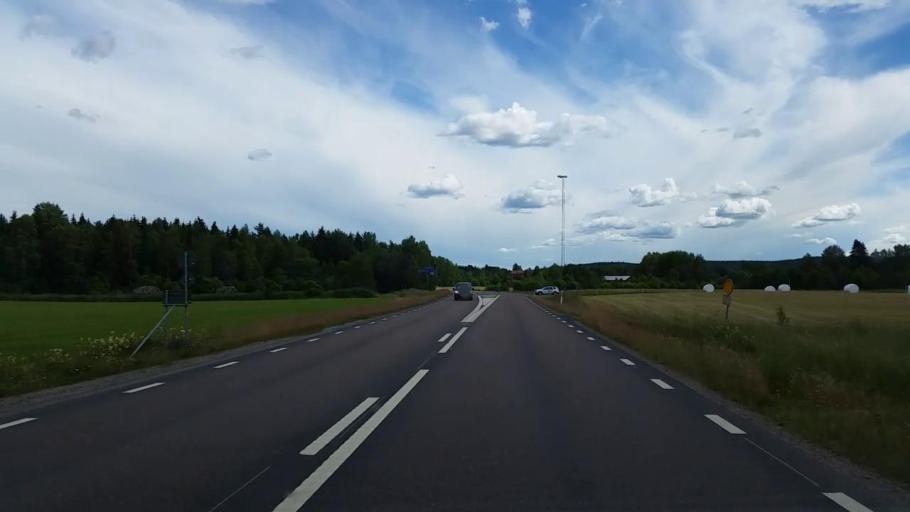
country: SE
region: Gaevleborg
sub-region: Ovanakers Kommun
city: Edsbyn
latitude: 61.3727
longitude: 15.8472
